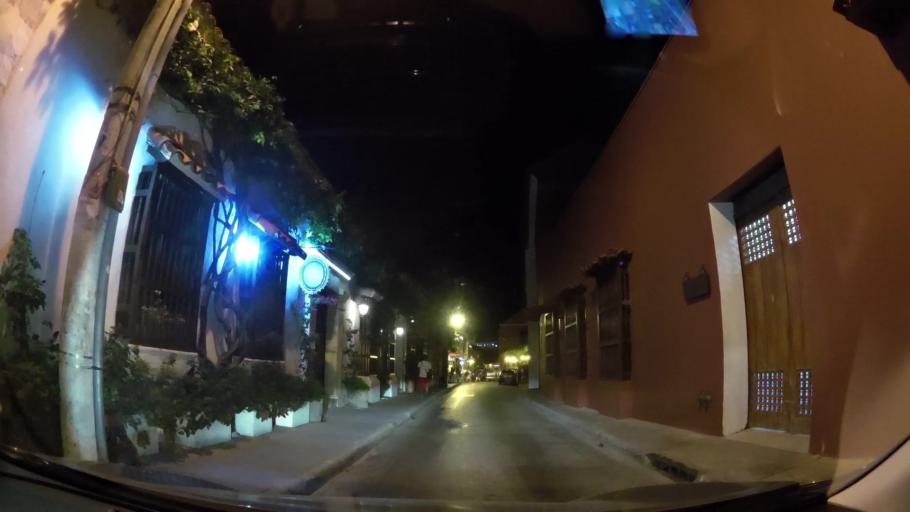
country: CO
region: Bolivar
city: Cartagena
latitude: 10.4280
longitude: -75.5469
